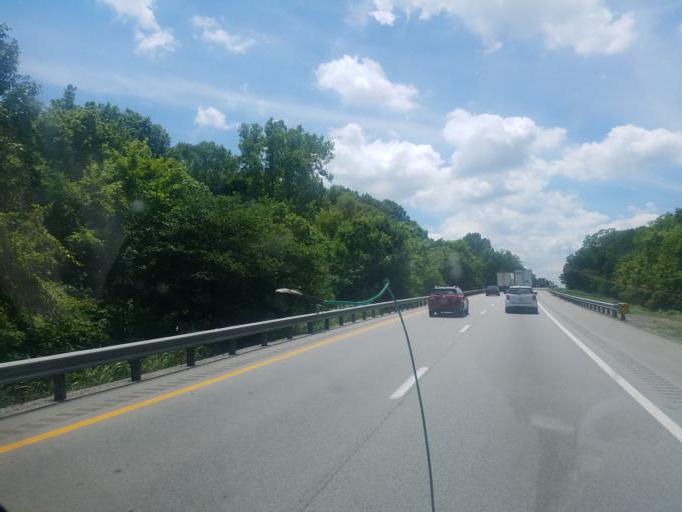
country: US
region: Kentucky
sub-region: Henry County
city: New Castle
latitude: 38.4746
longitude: -85.2746
